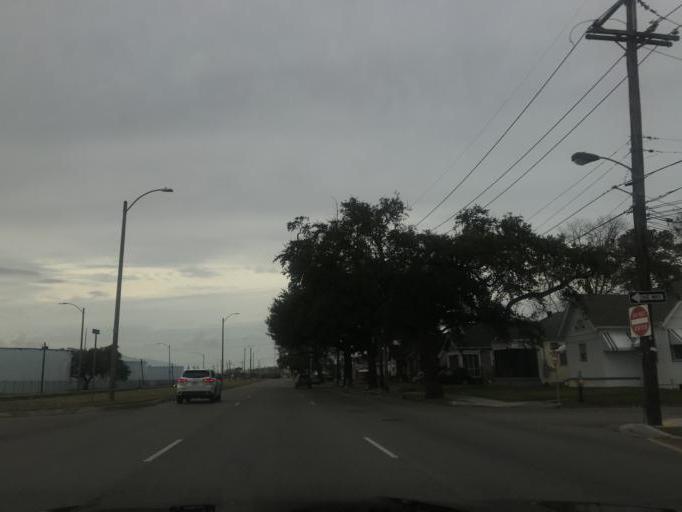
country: US
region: Louisiana
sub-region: Jefferson Parish
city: Jefferson
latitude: 29.9620
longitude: -90.1278
